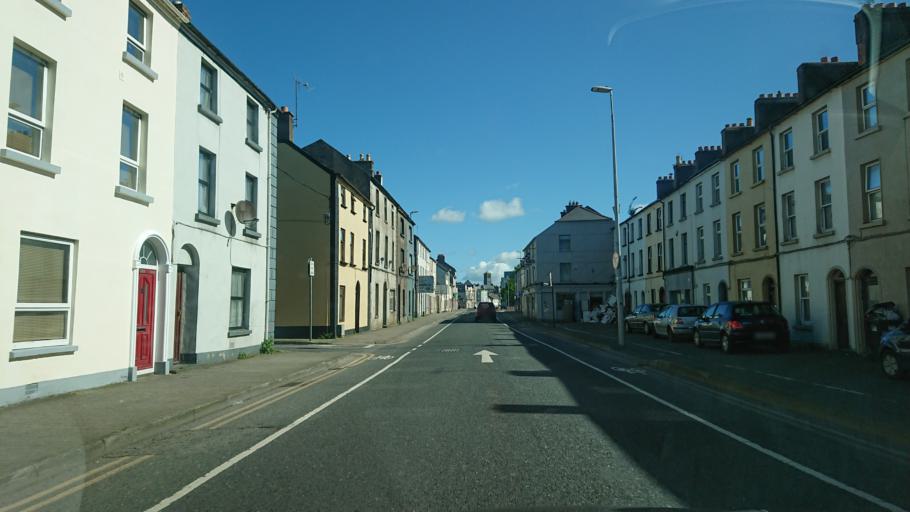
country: IE
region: Munster
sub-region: Waterford
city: Waterford
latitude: 52.2551
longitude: -7.1136
